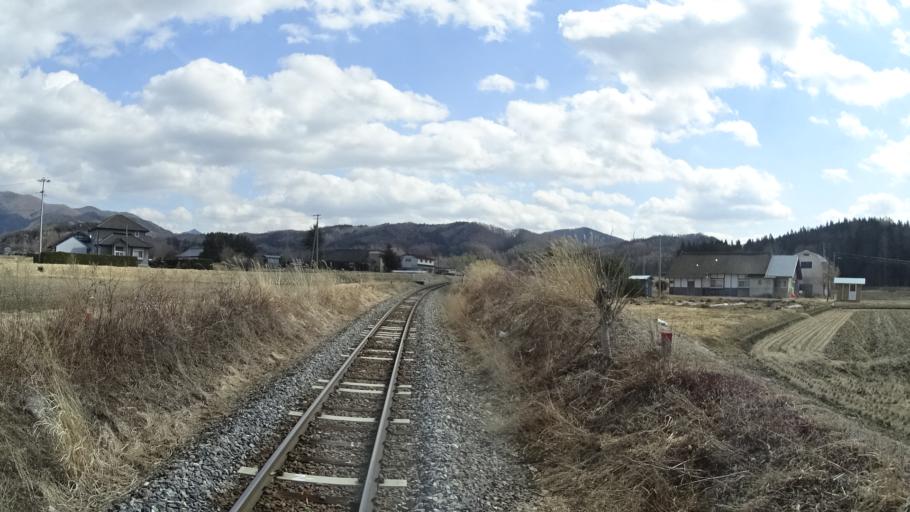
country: JP
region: Iwate
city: Tono
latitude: 39.2808
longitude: 141.5898
